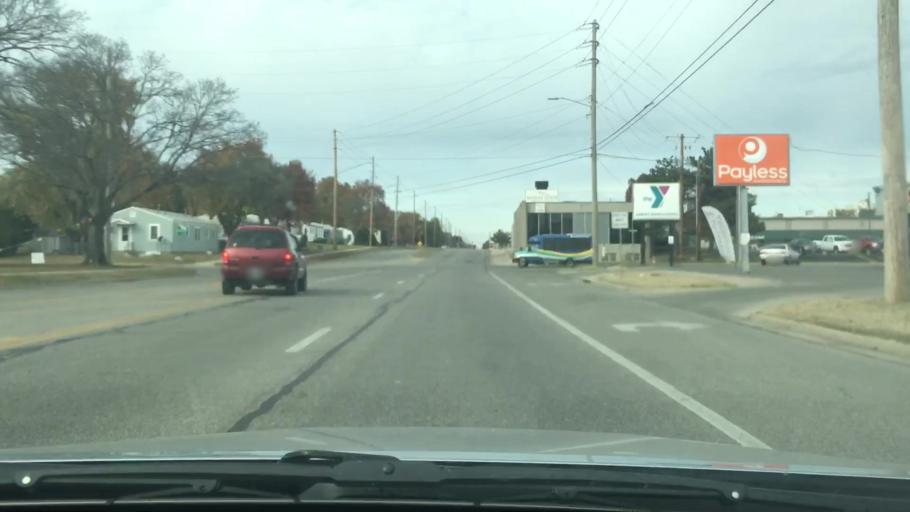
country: US
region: Kansas
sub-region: Sedgwick County
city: Wichita
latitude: 37.6659
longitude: -97.2804
